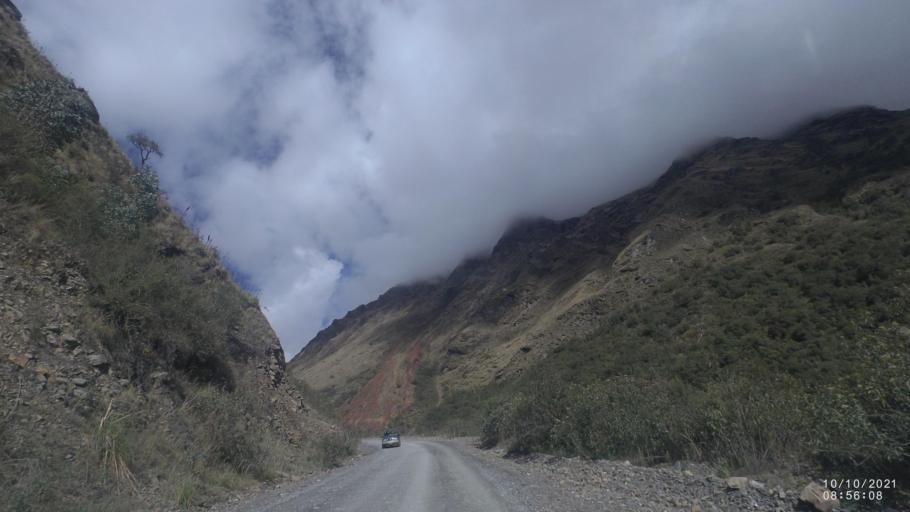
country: BO
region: La Paz
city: Quime
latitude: -16.9884
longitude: -67.2430
